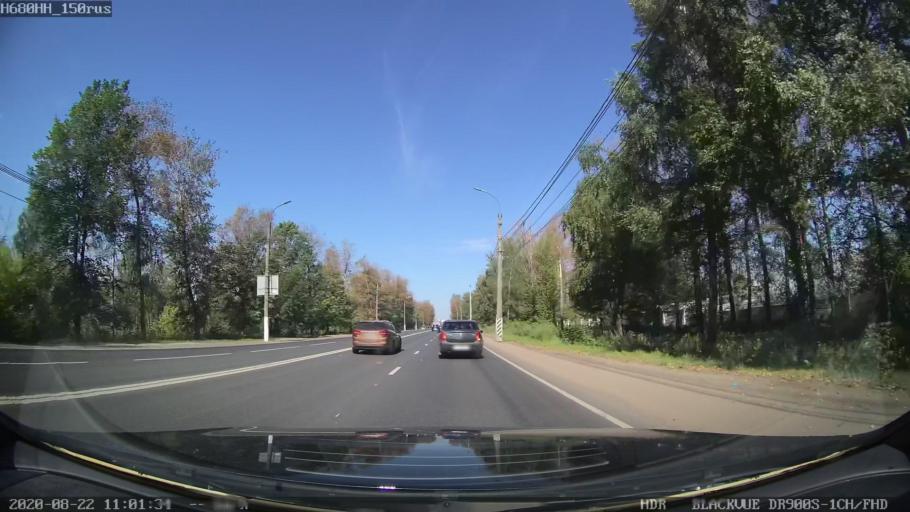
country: RU
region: Tverskaya
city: Tver
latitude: 56.8378
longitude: 35.9590
